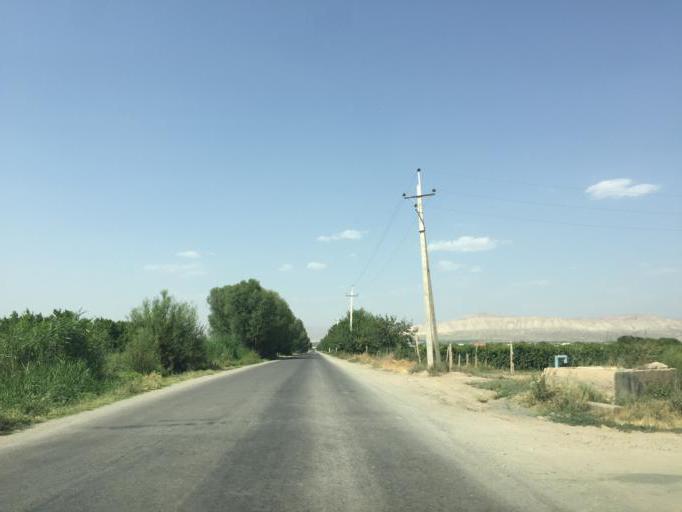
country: AM
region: Ararat
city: Shahumyan
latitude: 39.8899
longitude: 44.5940
